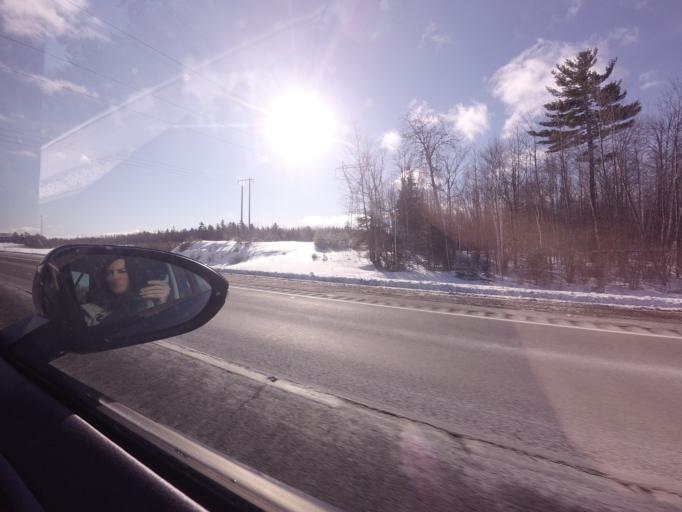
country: CA
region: New Brunswick
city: Fredericton
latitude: 45.8739
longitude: -66.6211
